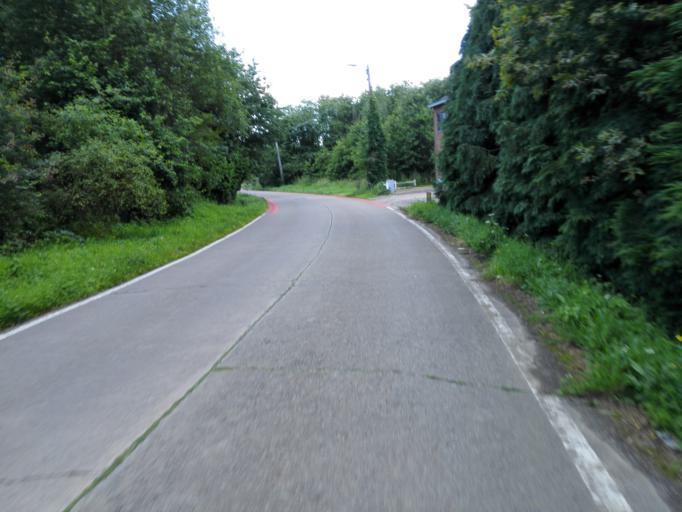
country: BE
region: Flanders
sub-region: Provincie Vlaams-Brabant
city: Tremelo
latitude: 50.9810
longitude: 4.7244
